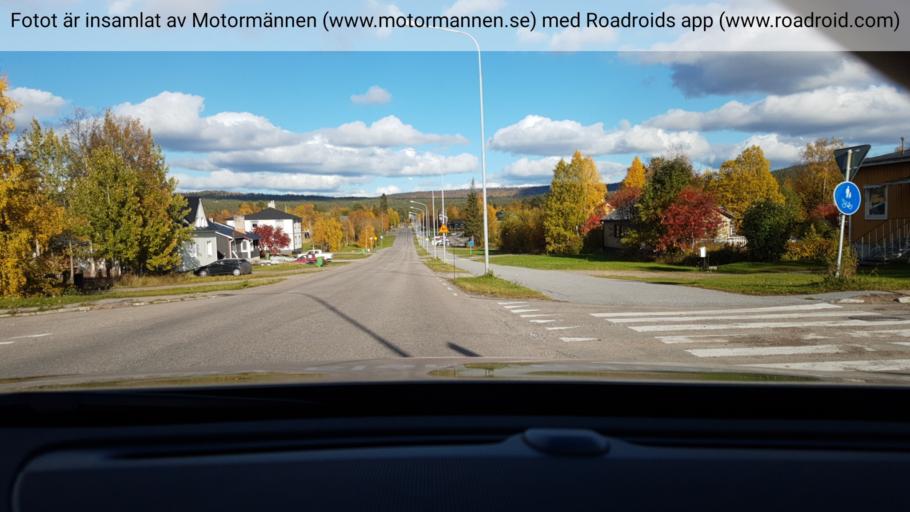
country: SE
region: Norrbotten
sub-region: Gallivare Kommun
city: Malmberget
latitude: 67.1861
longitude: 20.7405
